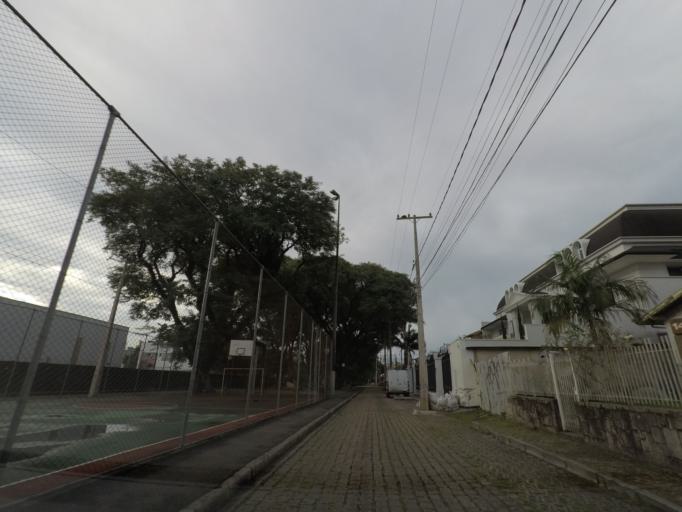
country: BR
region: Parana
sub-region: Curitiba
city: Curitiba
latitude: -25.4222
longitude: -49.2496
